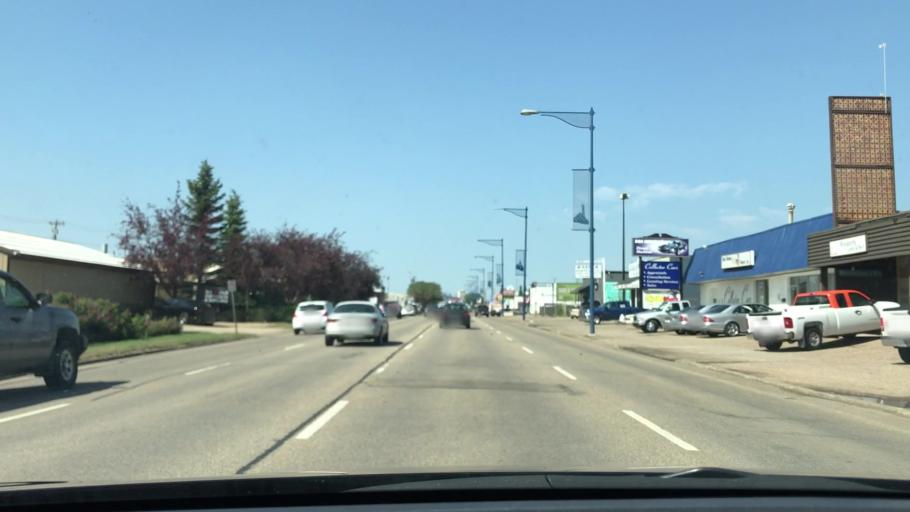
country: CA
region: Alberta
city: Edmonton
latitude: 53.4933
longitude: -113.4920
